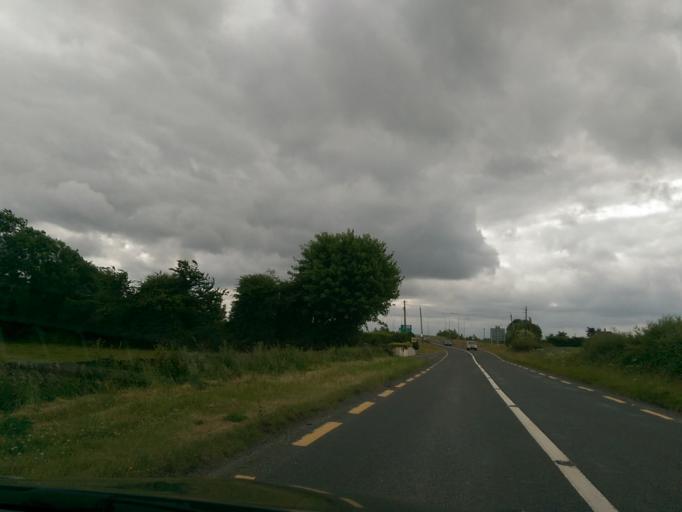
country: IE
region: Munster
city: Thurles
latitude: 52.6269
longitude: -7.7773
